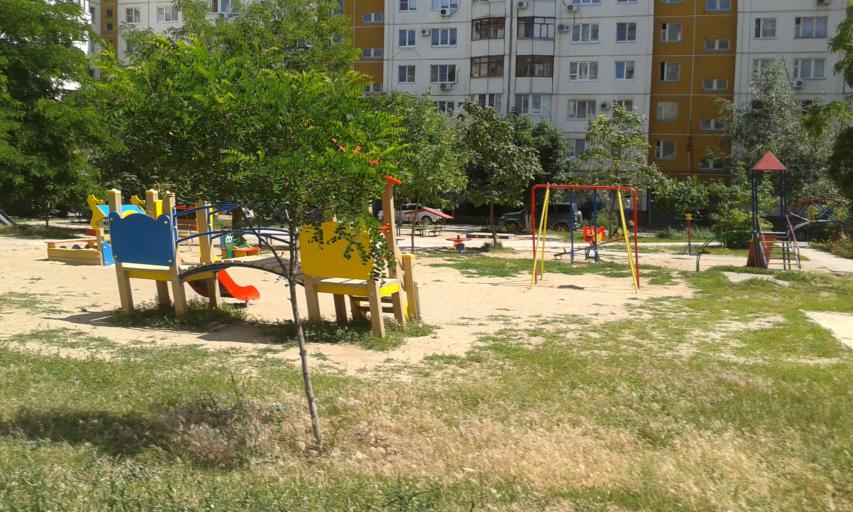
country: RU
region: Volgograd
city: Volgograd
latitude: 48.7548
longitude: 44.5079
